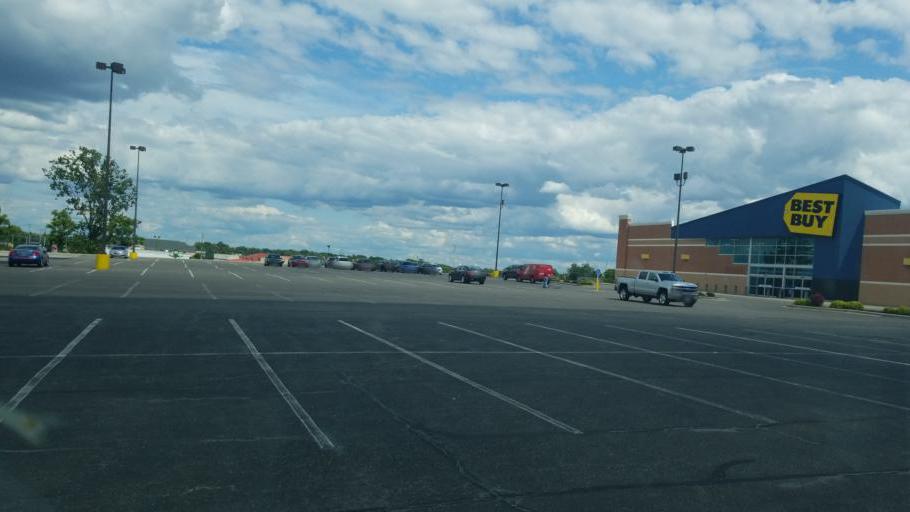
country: US
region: Ohio
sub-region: Richland County
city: Ontario
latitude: 40.7867
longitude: -82.5934
